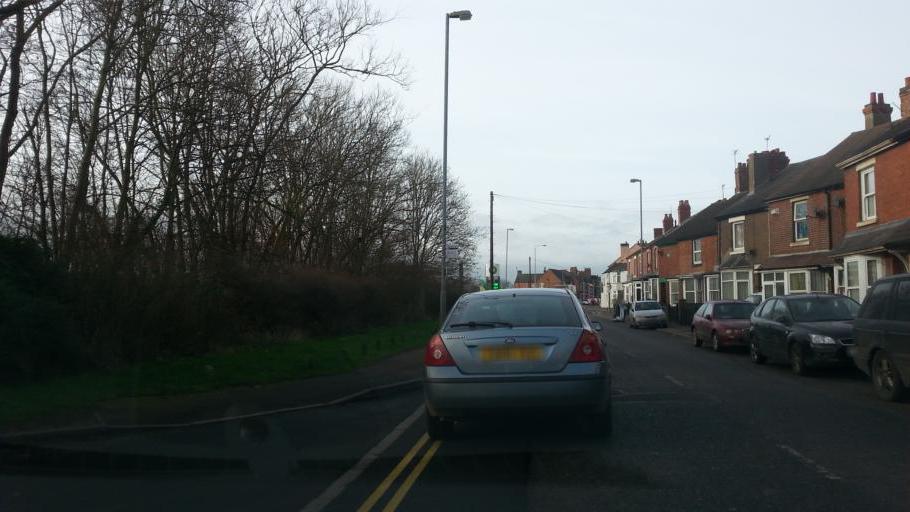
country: GB
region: England
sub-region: Leicestershire
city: Melton Mowbray
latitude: 52.7683
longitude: -0.8738
